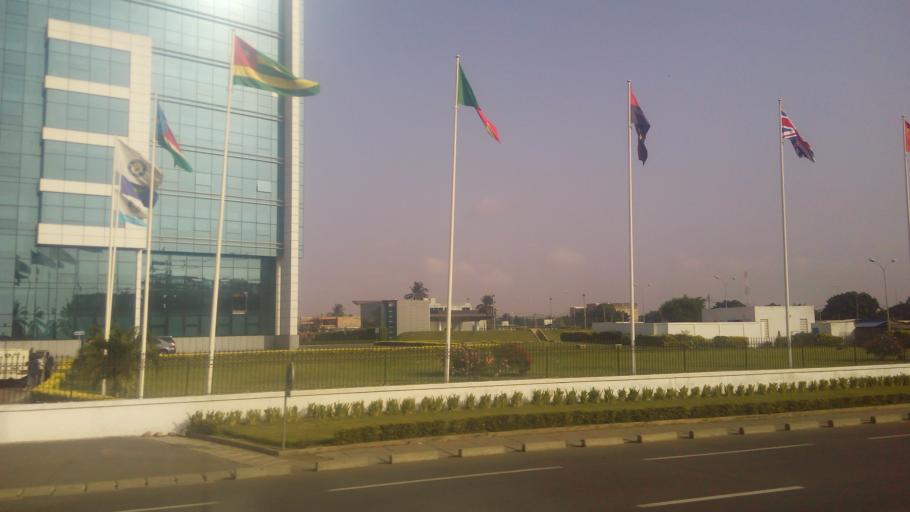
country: TG
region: Maritime
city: Lome
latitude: 6.1352
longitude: 1.2588
